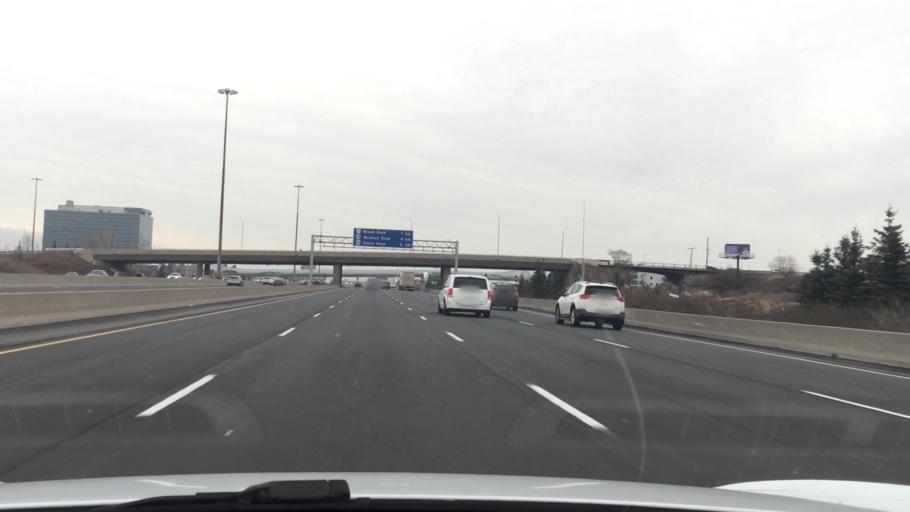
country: CA
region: Ontario
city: Ajax
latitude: 43.8290
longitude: -79.0907
